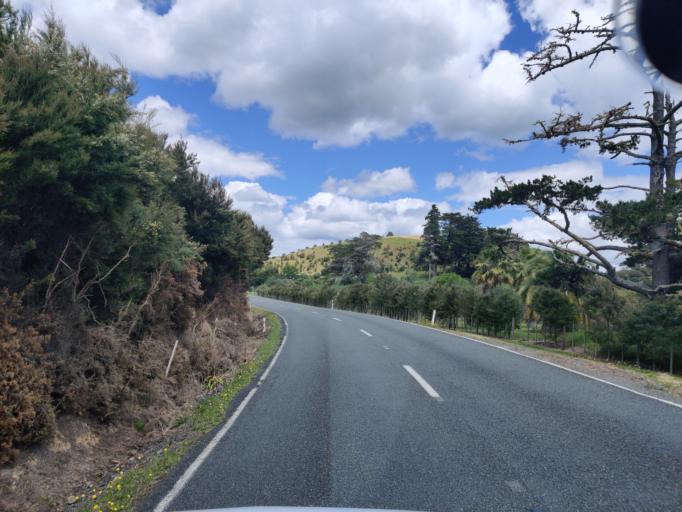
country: NZ
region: Northland
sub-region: Far North District
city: Paihia
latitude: -35.2766
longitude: 174.1396
